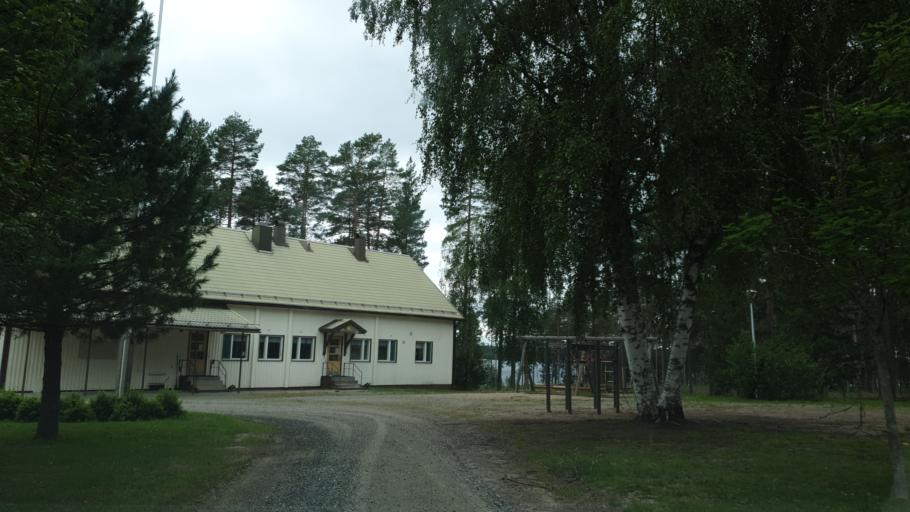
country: FI
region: Kainuu
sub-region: Kehys-Kainuu
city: Kuhmo
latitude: 64.1934
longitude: 29.1651
